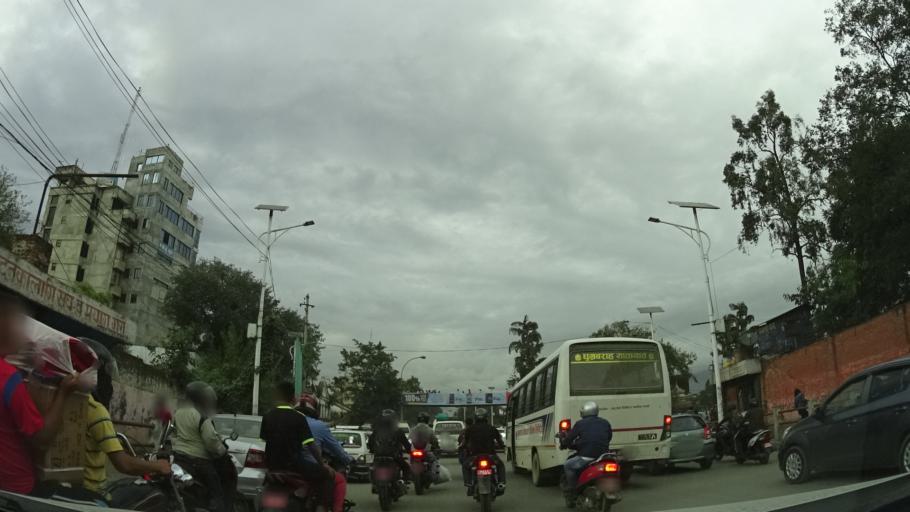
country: NP
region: Central Region
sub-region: Bagmati Zone
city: Kathmandu
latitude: 27.7064
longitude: 85.3141
